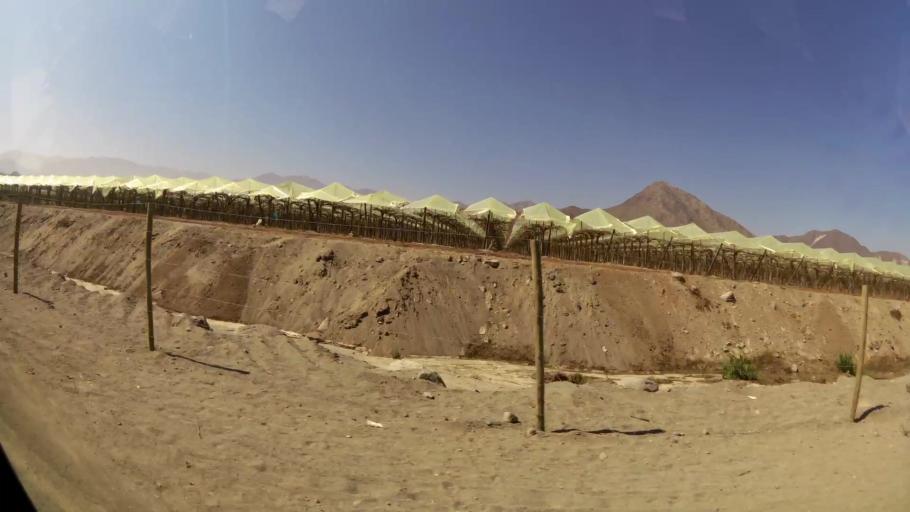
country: PE
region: Ica
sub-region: Provincia de Ica
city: San Juan Bautista
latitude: -13.9489
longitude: -75.6833
